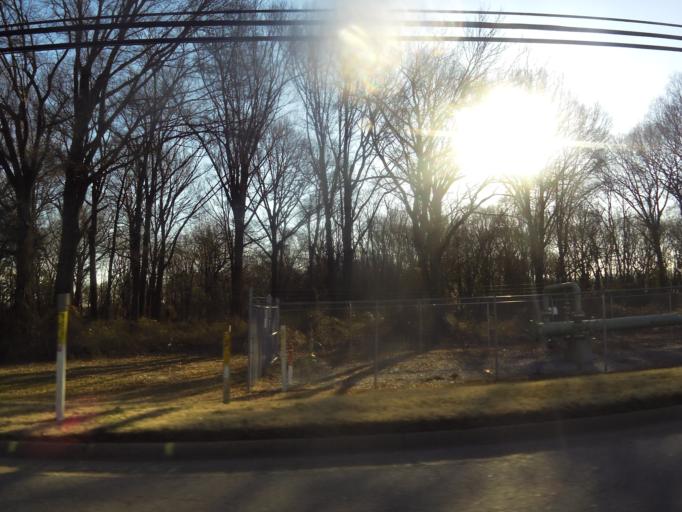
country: US
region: Virginia
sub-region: City of Hopewell
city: Hopewell
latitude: 37.2968
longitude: -77.2788
